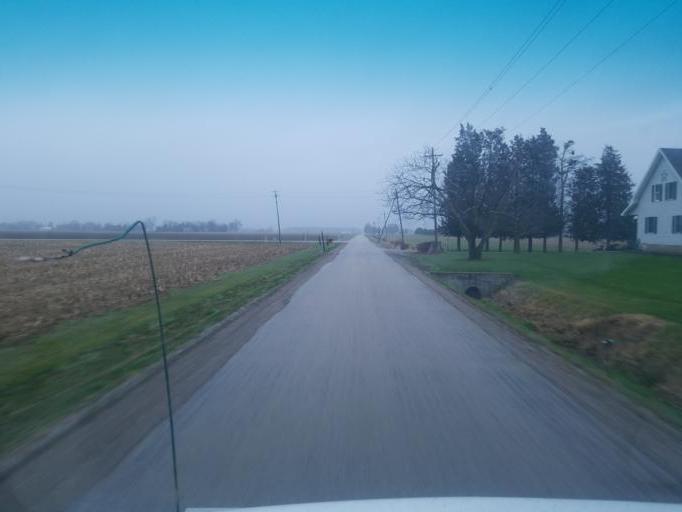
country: US
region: Ohio
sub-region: Fulton County
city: Archbold
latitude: 41.4278
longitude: -84.2534
